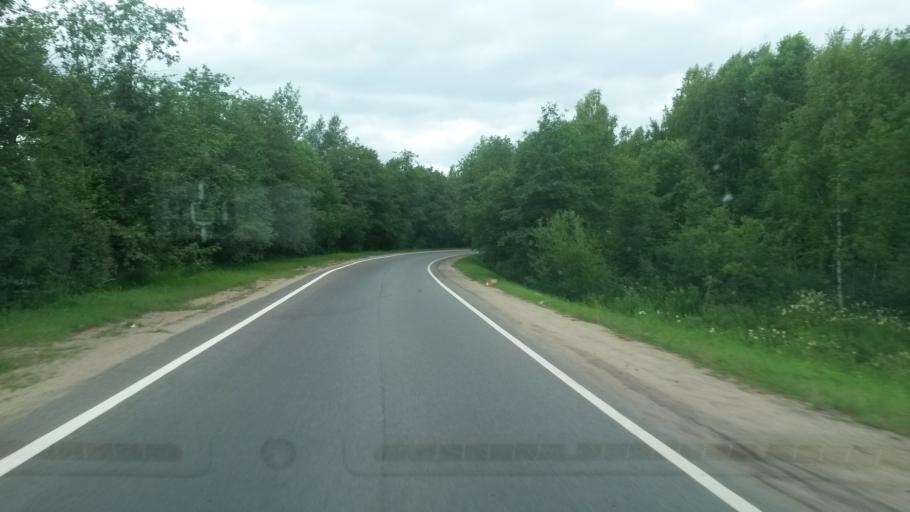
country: RU
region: Jaroslavl
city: Krasnyye Tkachi
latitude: 57.4042
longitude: 39.6588
